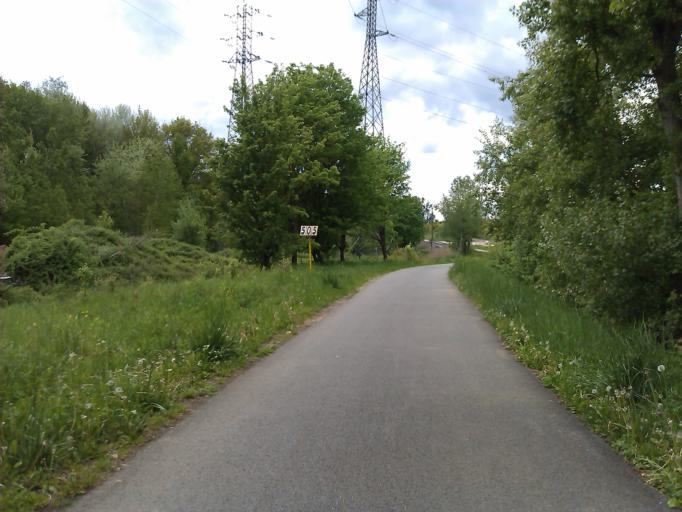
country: FR
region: Franche-Comte
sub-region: Departement du Doubs
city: Sochaux
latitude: 47.5035
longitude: 6.8278
